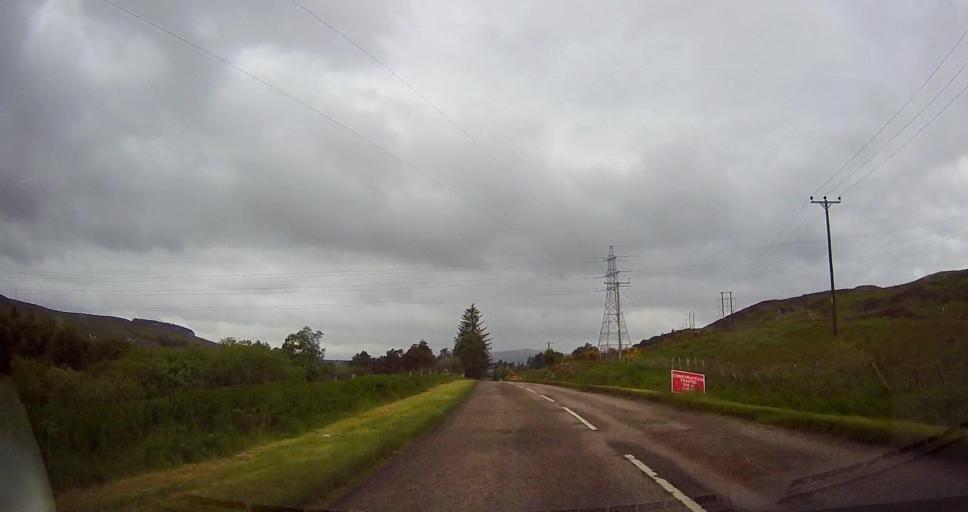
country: GB
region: Scotland
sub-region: Highland
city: Alness
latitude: 58.0190
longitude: -4.3488
